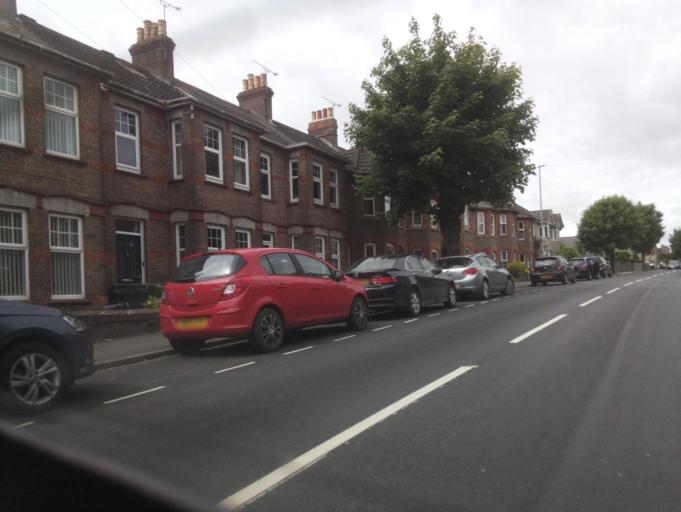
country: GB
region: England
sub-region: Dorset
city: Dorchester
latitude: 50.7114
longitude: -2.4467
